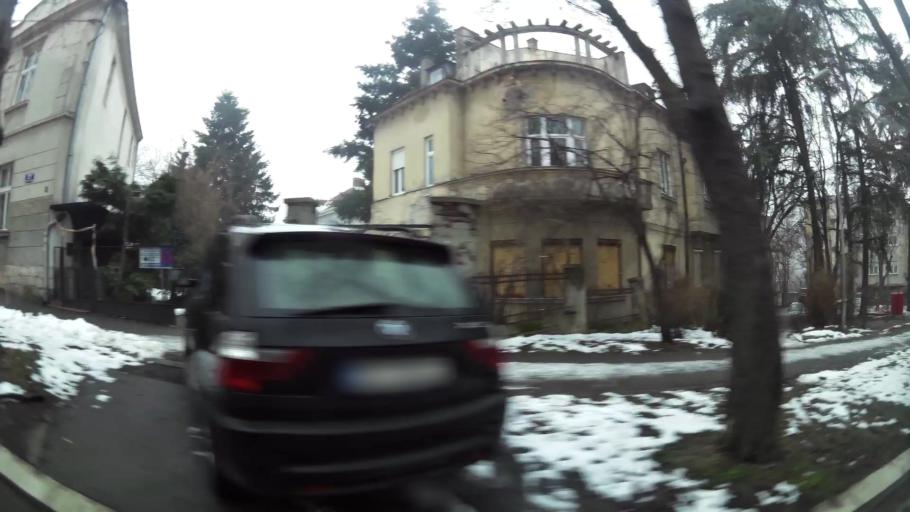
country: RS
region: Central Serbia
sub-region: Belgrade
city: Savski Venac
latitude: 44.7939
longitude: 20.4423
